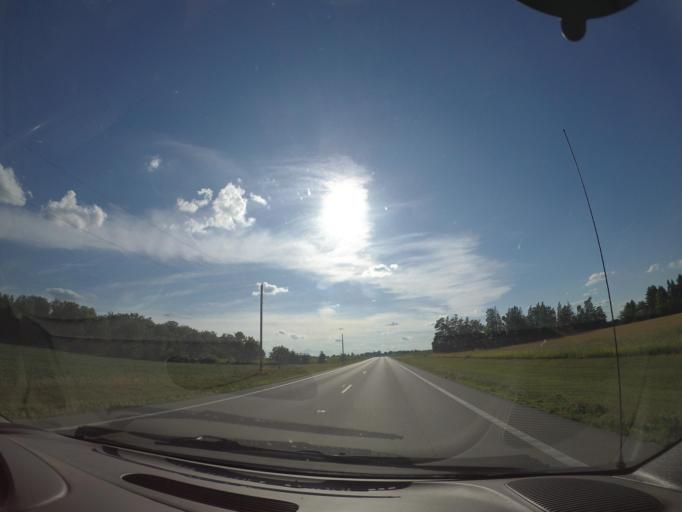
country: US
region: Ohio
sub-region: Henry County
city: Napoleon
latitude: 41.4319
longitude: -84.2199
